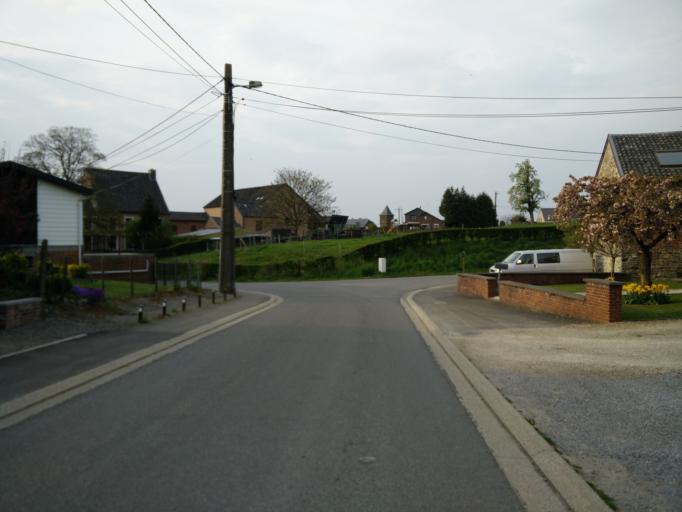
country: BE
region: Wallonia
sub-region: Province de Liege
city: Dalhem
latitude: 50.7338
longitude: 5.7715
